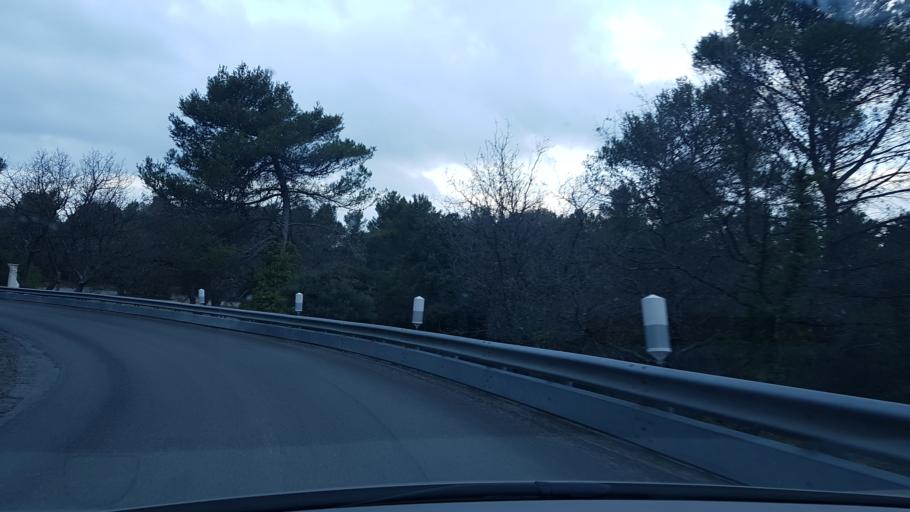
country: FR
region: Provence-Alpes-Cote d'Azur
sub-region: Departement des Bouches-du-Rhone
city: Mimet
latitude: 43.4301
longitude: 5.5096
